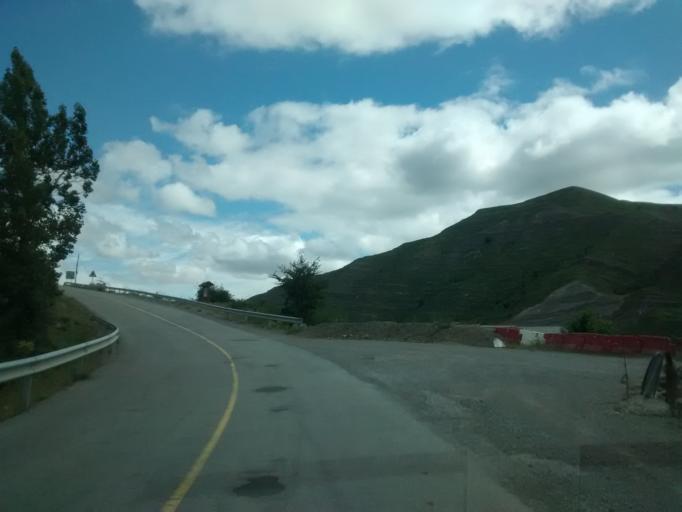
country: ES
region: La Rioja
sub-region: Provincia de La Rioja
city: Terroba
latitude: 42.2625
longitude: -2.4343
